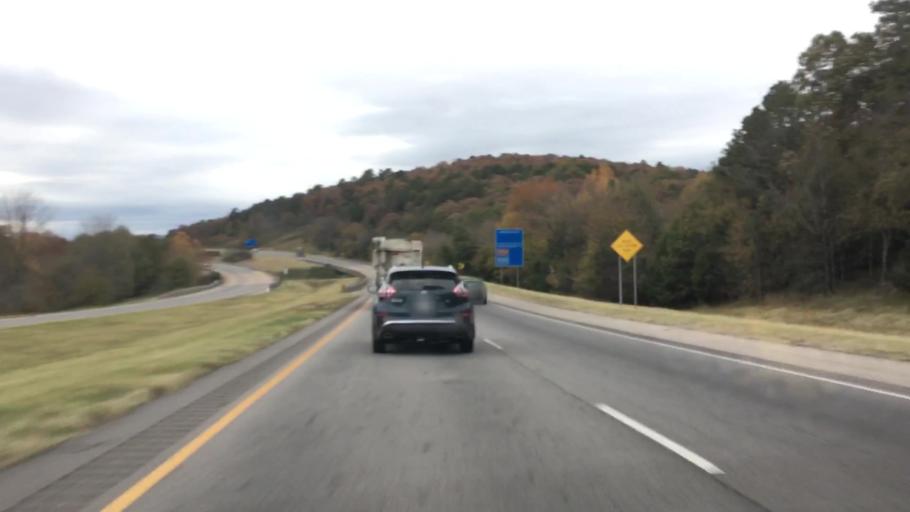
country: US
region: Arkansas
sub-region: Johnson County
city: Coal Hill
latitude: 35.5023
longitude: -93.7275
